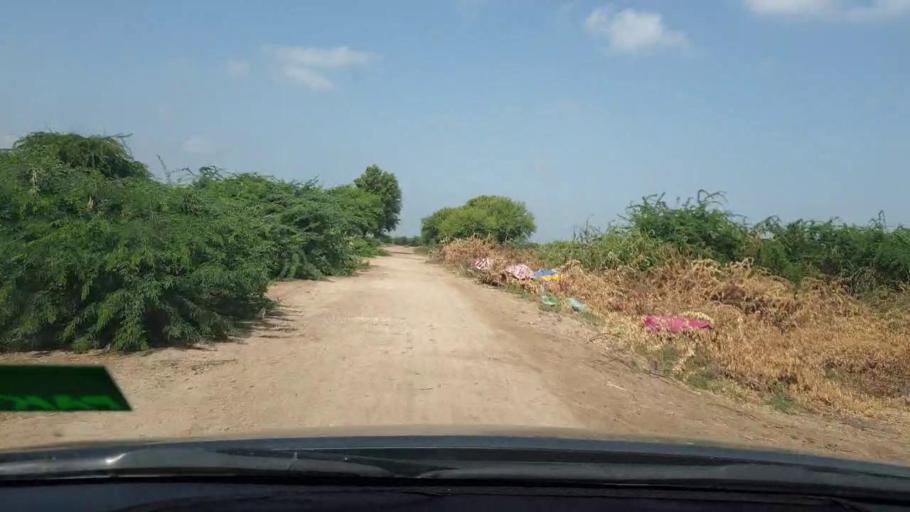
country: PK
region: Sindh
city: Tando Bago
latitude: 24.9392
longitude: 69.0494
